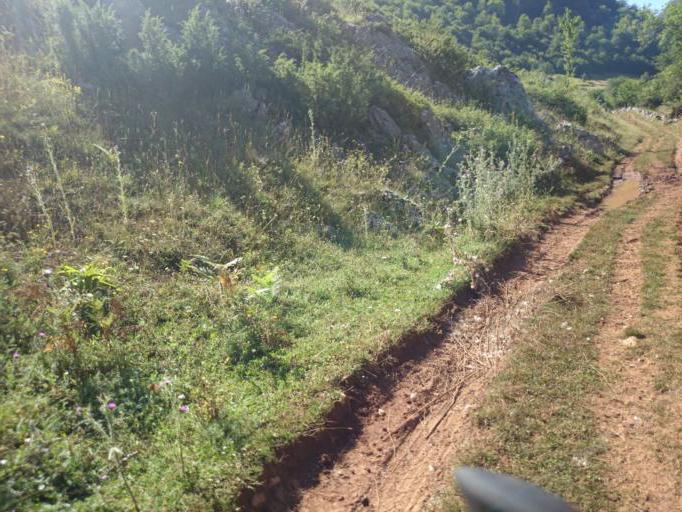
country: AL
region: Diber
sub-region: Rrethi i Bulqizes
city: Martanesh
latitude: 41.3897
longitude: 20.1563
